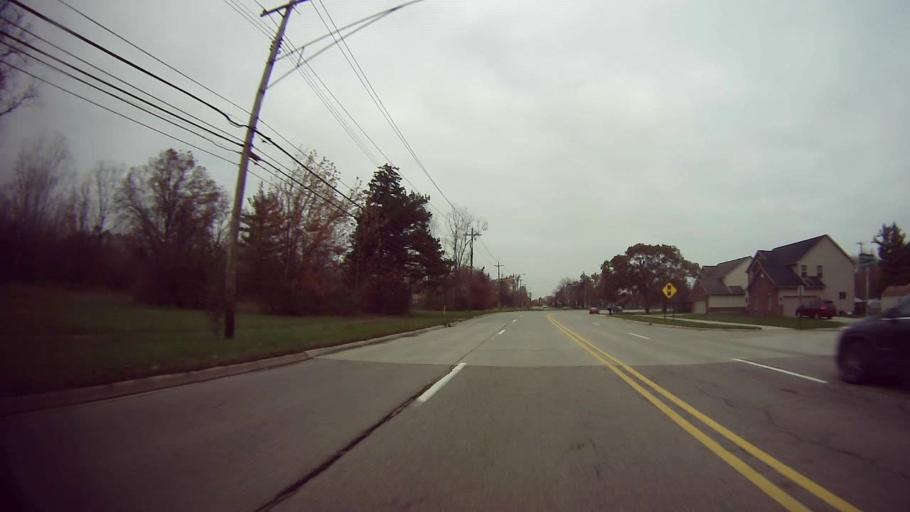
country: US
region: Michigan
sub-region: Oakland County
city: Clawson
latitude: 42.5532
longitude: -83.1310
